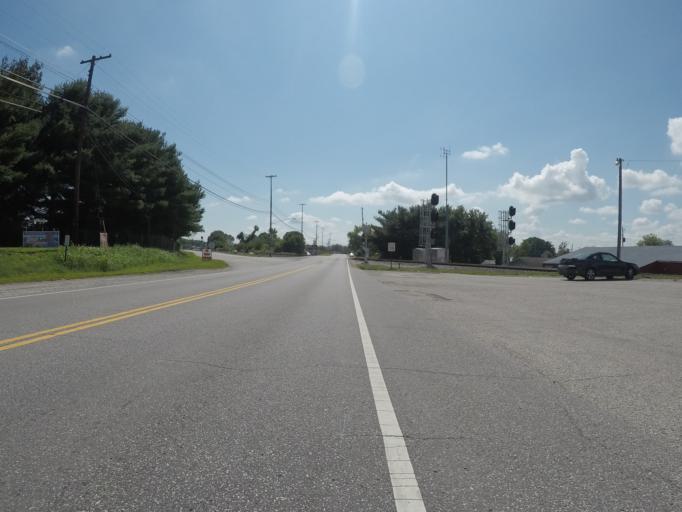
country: US
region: Ohio
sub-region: Lawrence County
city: South Point
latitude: 38.4226
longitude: -82.5900
